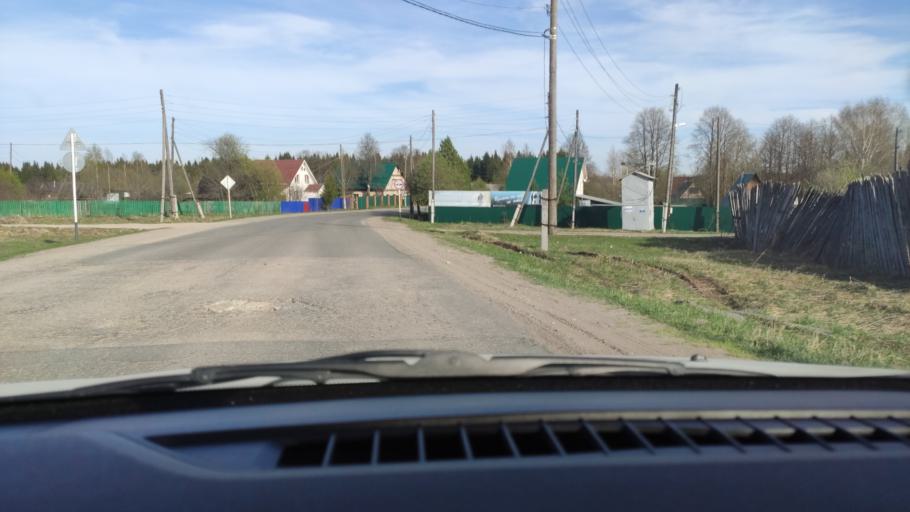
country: RU
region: Perm
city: Novyye Lyady
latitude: 57.9413
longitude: 56.5819
